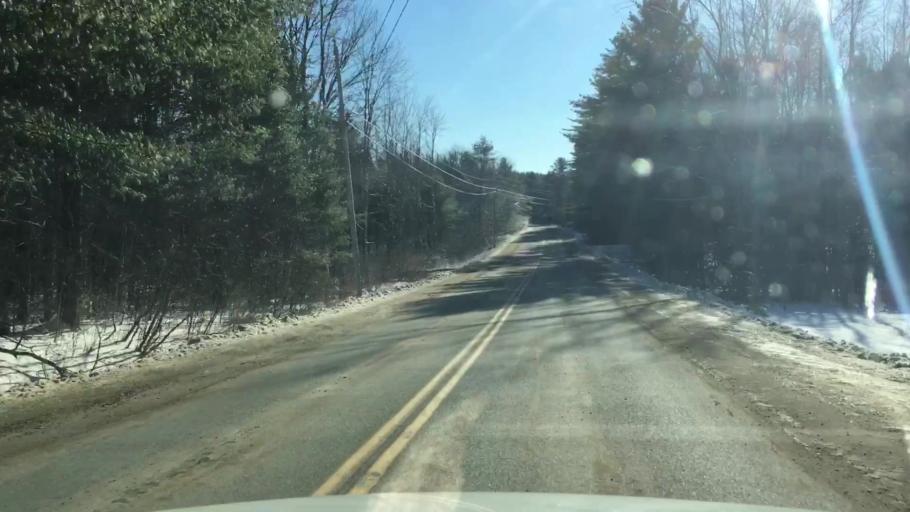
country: US
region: Maine
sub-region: Kennebec County
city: Readfield
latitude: 44.3584
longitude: -69.9910
